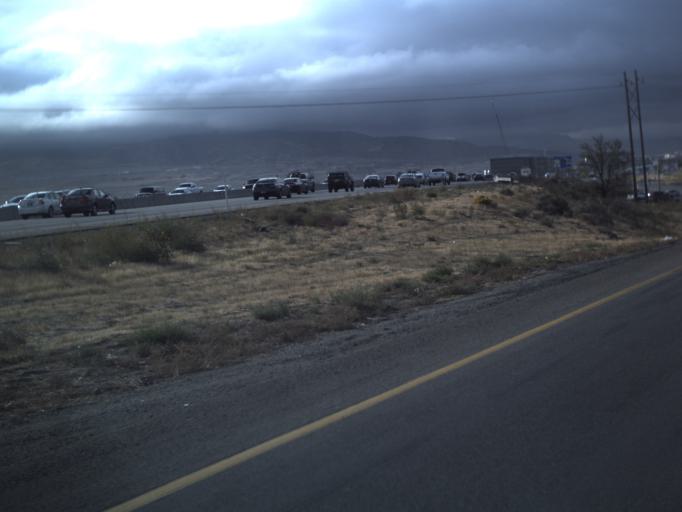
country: US
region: Utah
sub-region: Utah County
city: Lehi
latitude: 40.4127
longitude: -111.8664
